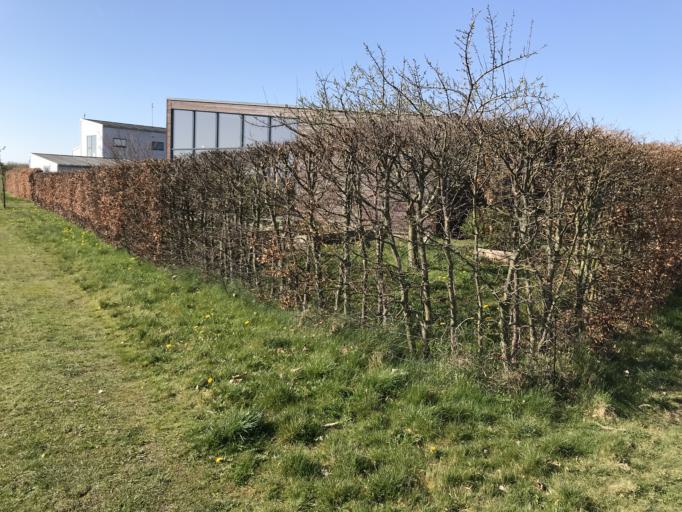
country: DK
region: Capital Region
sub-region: Hoje-Taastrup Kommune
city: Flong
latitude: 55.6594
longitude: 12.1524
